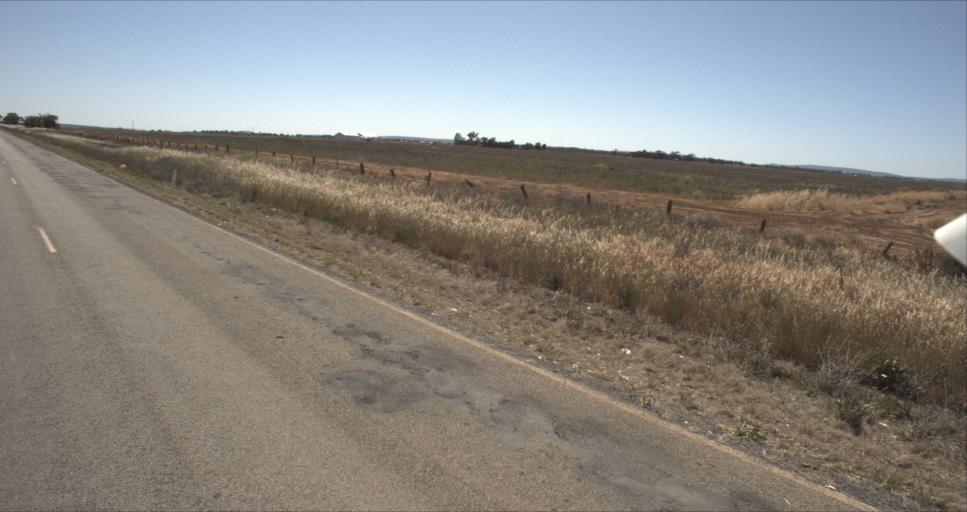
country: AU
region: New South Wales
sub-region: Leeton
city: Leeton
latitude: -34.5105
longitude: 146.2852
